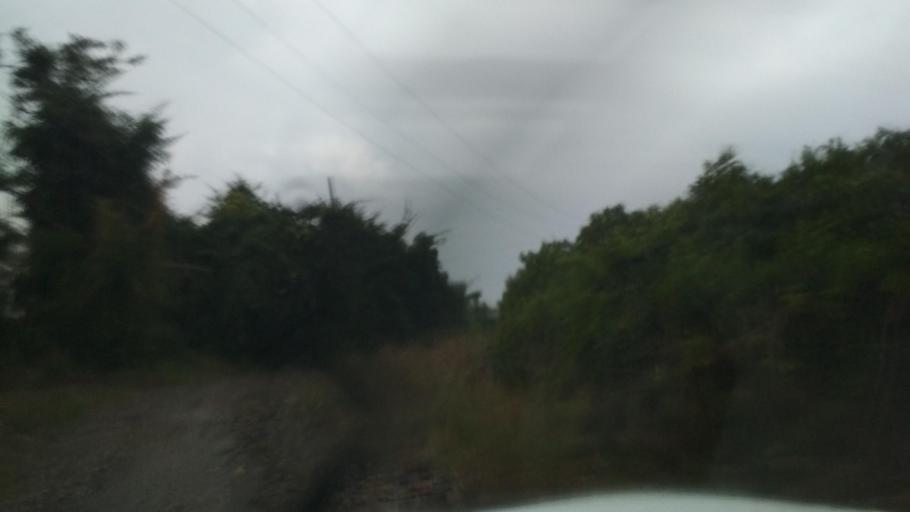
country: MM
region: Shan
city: Taunggyi
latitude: 20.3000
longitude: 97.3025
